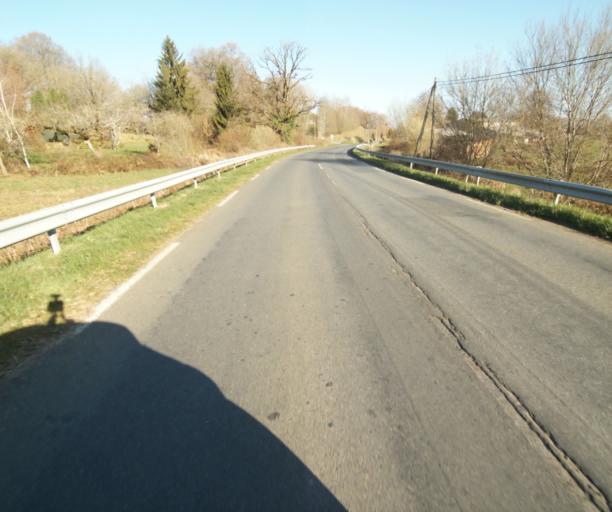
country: FR
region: Limousin
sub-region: Departement de la Correze
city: Uzerche
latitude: 45.3919
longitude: 1.5947
